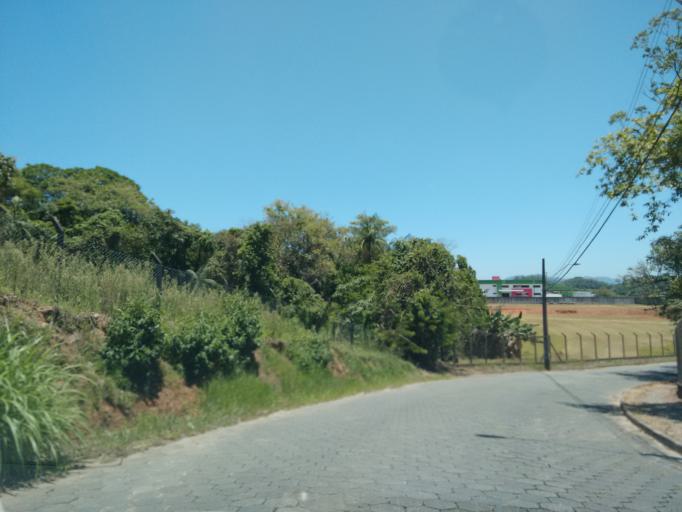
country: BR
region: Santa Catarina
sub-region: Blumenau
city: Blumenau
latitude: -26.8828
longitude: -49.1361
